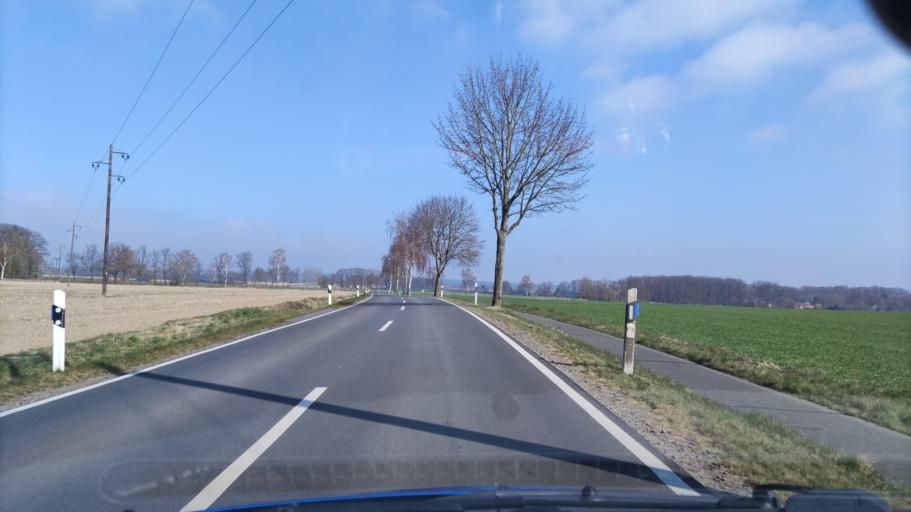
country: DE
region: Lower Saxony
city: Waddeweitz
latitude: 52.9733
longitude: 10.9721
